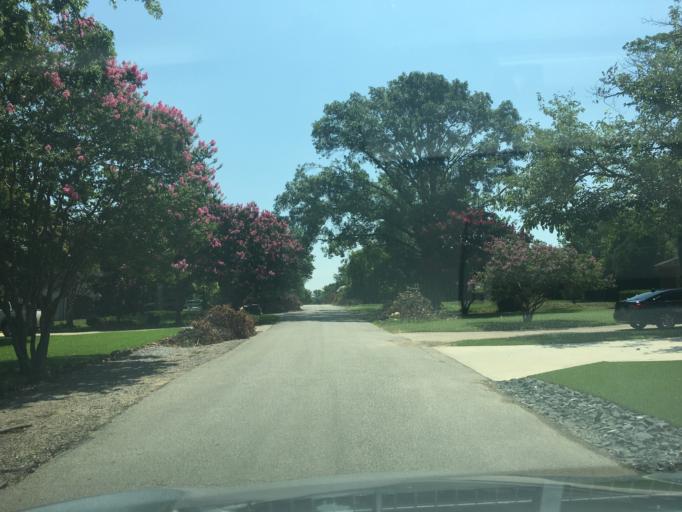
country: US
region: Texas
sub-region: Dallas County
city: Addison
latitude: 32.9183
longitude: -96.7964
